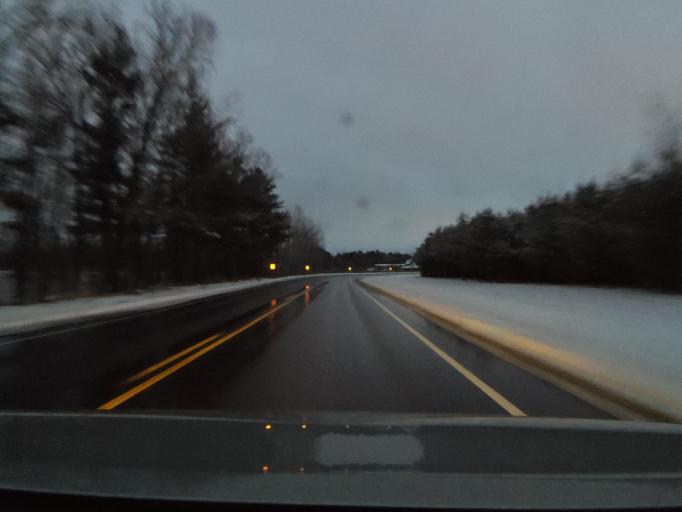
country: US
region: Wisconsin
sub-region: Dunn County
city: Menomonie
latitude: 44.9183
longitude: -91.9491
